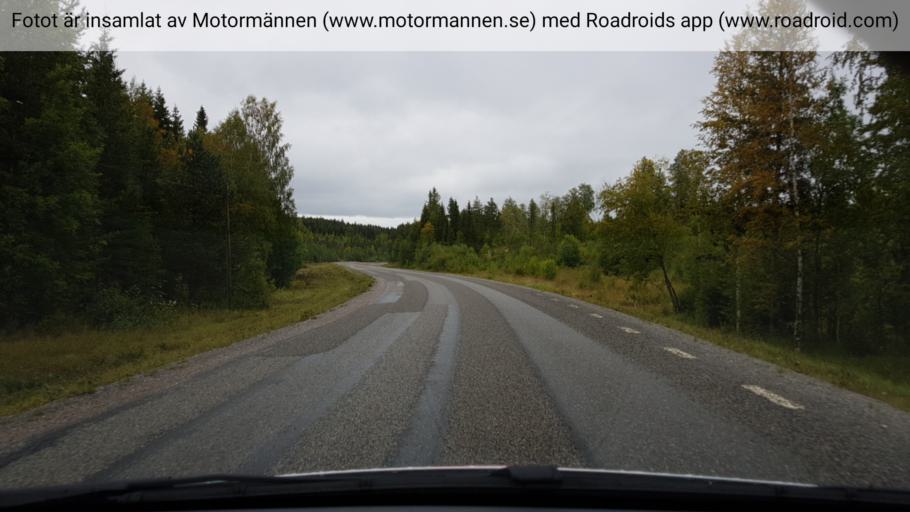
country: SE
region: Vaesterbotten
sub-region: Dorotea Kommun
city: Dorotea
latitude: 63.8372
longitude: 16.1525
